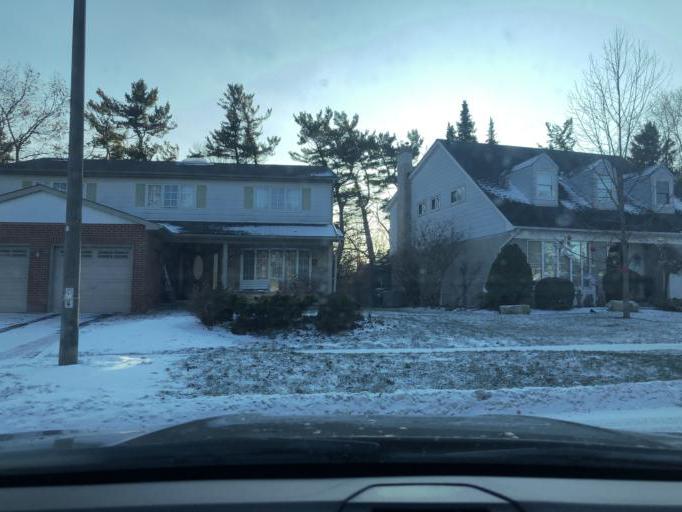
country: CA
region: Ontario
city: Scarborough
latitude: 43.7738
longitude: -79.1478
